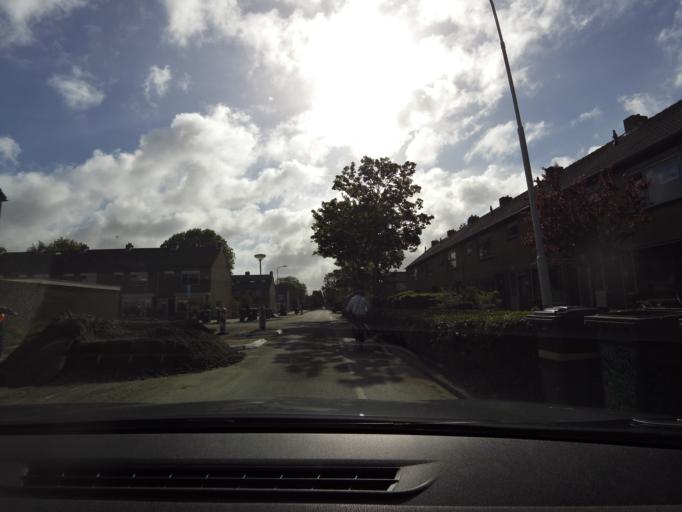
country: NL
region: Zeeland
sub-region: Schouwen-Duiveland
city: Scharendijke
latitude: 51.6490
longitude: 3.9031
